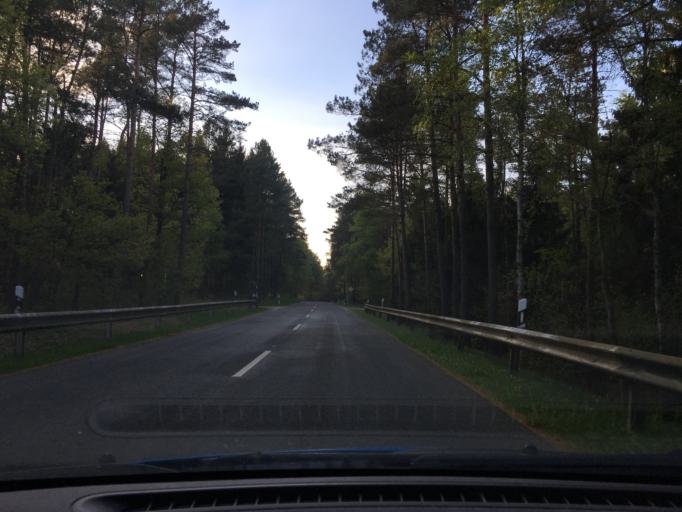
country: DE
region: Lower Saxony
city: Bispingen
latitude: 53.0015
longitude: 9.9991
